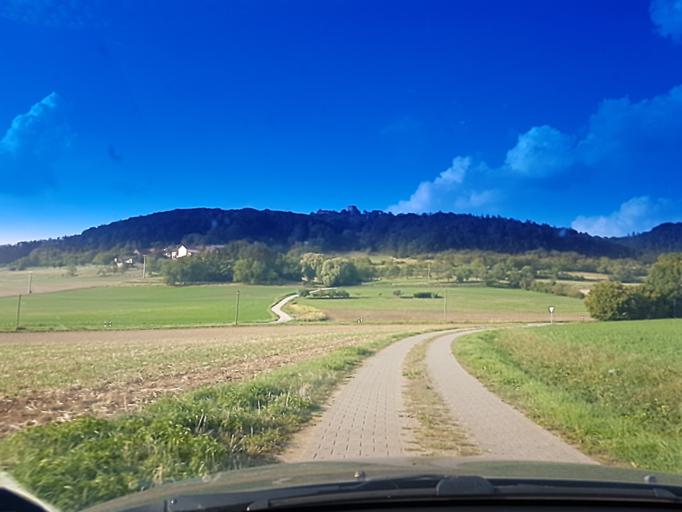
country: DE
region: Bavaria
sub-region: Upper Franconia
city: Schesslitz
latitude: 49.9455
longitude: 11.0494
